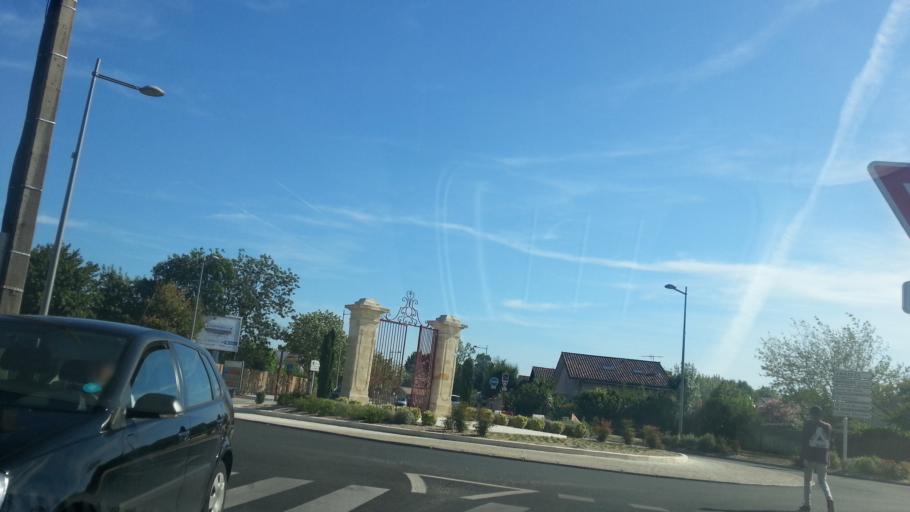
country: FR
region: Aquitaine
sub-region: Departement de la Gironde
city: Bassens
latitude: 44.8962
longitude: -0.5165
